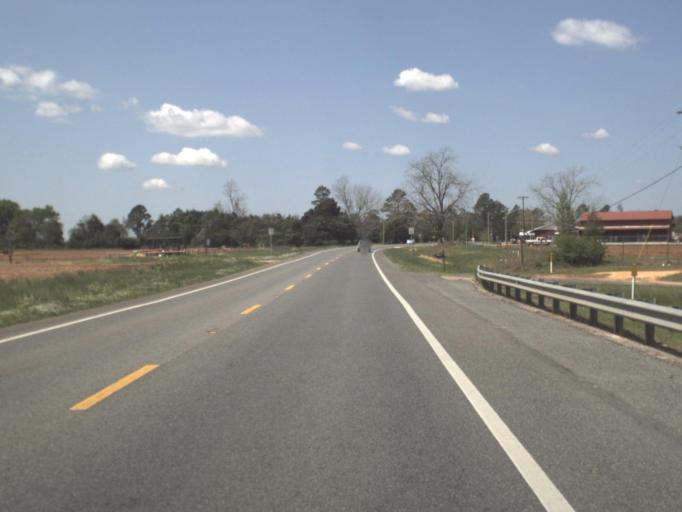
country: US
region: Florida
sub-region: Escambia County
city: Century
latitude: 30.9493
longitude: -87.1743
